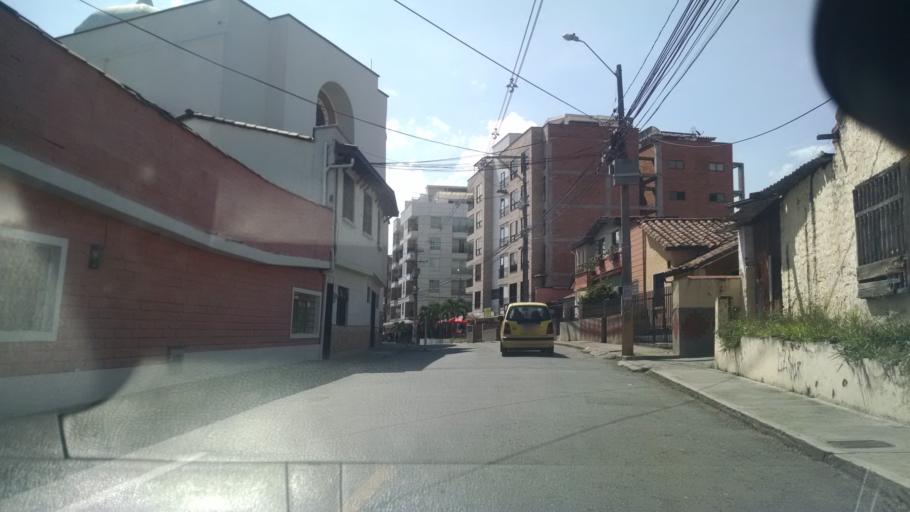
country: CO
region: Antioquia
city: Medellin
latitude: 6.2566
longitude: -75.6027
